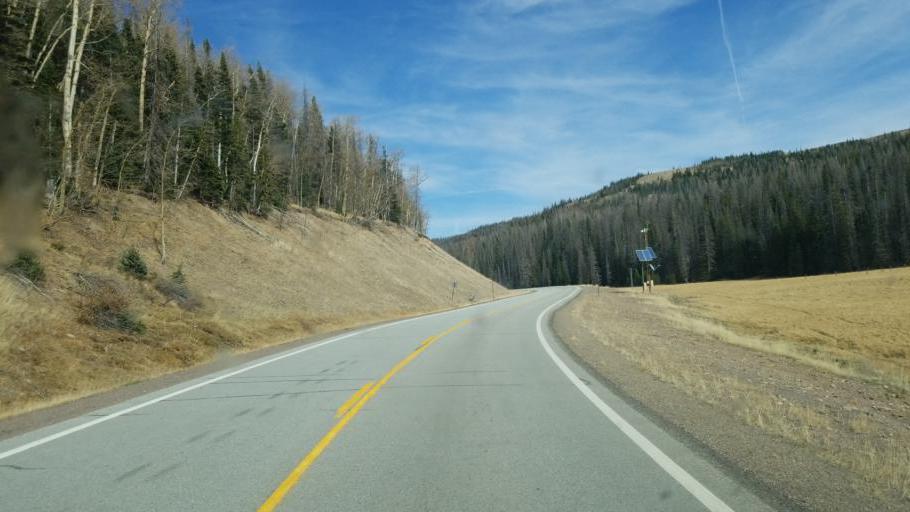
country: US
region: New Mexico
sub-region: Rio Arriba County
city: Chama
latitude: 37.0772
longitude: -106.3880
